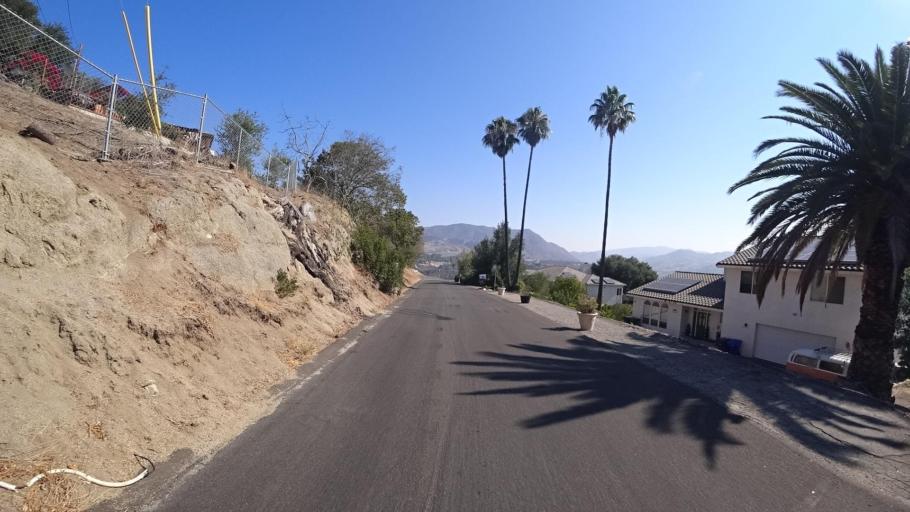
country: US
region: California
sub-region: San Diego County
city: Fallbrook
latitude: 33.4030
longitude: -117.2320
